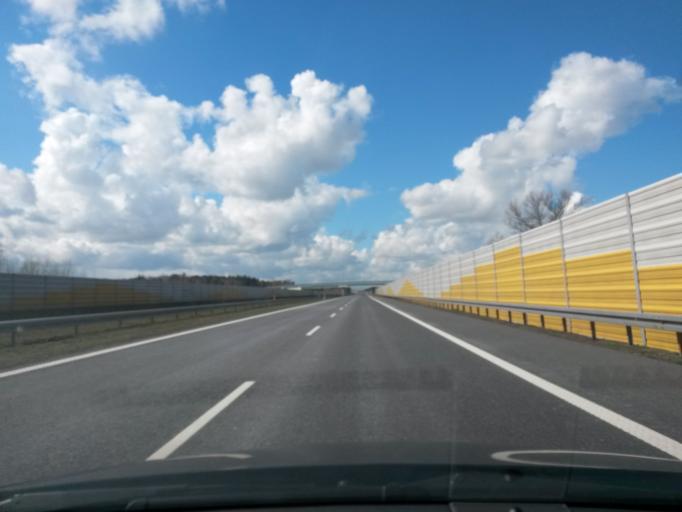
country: PL
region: Lodz Voivodeship
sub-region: Powiat leczycki
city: Swinice Warckie
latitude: 52.0177
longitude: 18.9418
